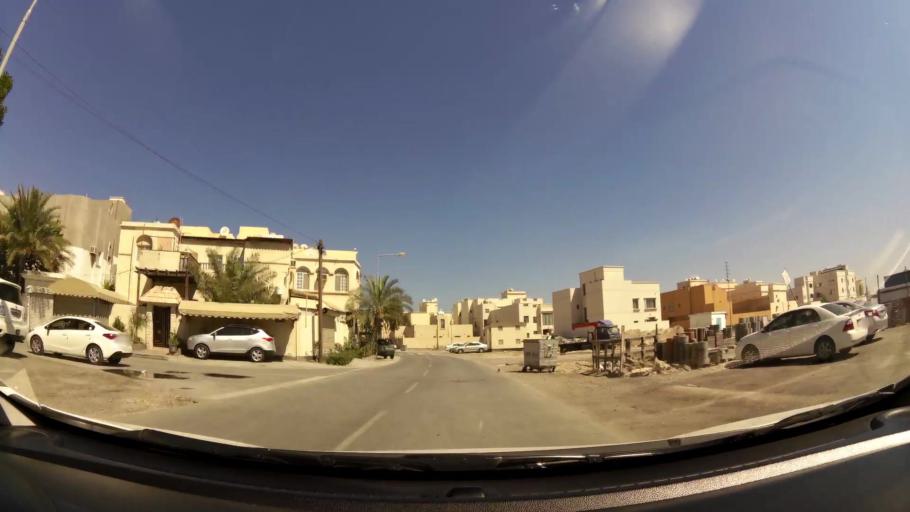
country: BH
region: Muharraq
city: Al Muharraq
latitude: 26.2782
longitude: 50.6361
